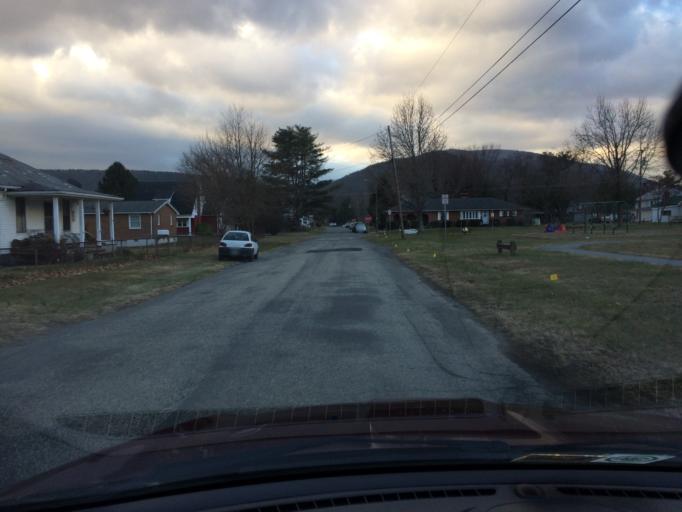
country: US
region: Virginia
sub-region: Alleghany County
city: Clifton Forge
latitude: 37.8245
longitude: -79.8193
